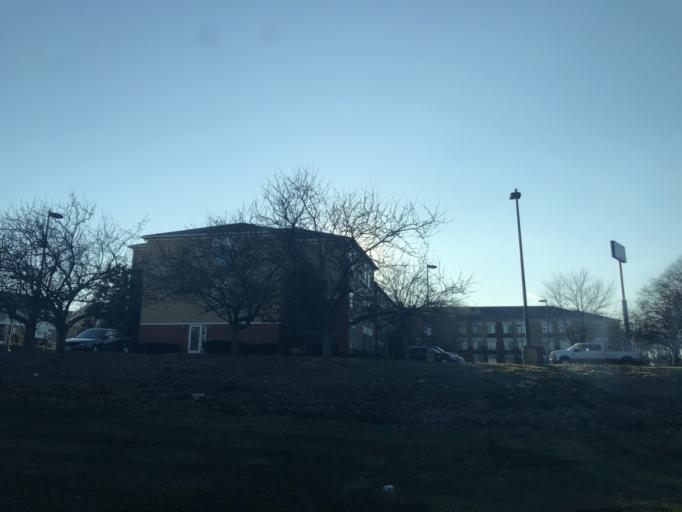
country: US
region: New Jersey
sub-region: Middlesex County
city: Fords
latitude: 40.5389
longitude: -74.2986
